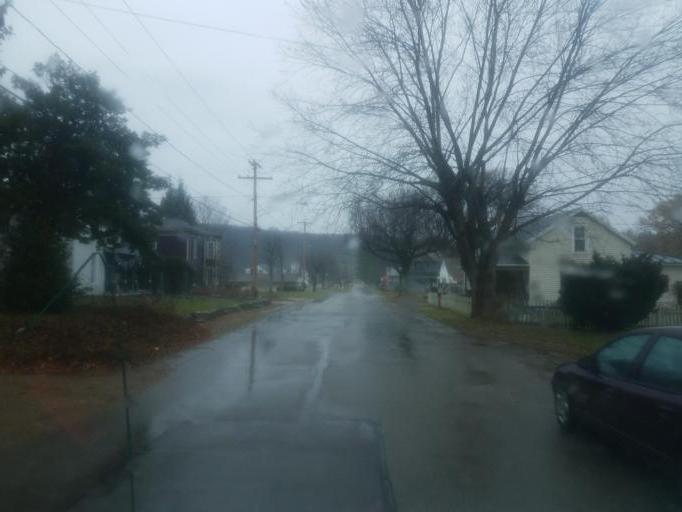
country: US
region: Ohio
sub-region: Sandusky County
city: Bellville
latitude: 40.6213
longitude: -82.5151
